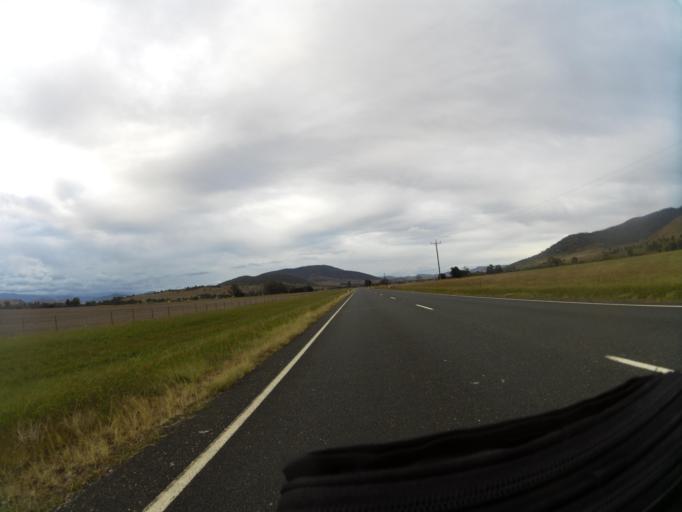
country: AU
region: New South Wales
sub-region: Snowy River
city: Jindabyne
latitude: -36.1069
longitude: 147.9800
